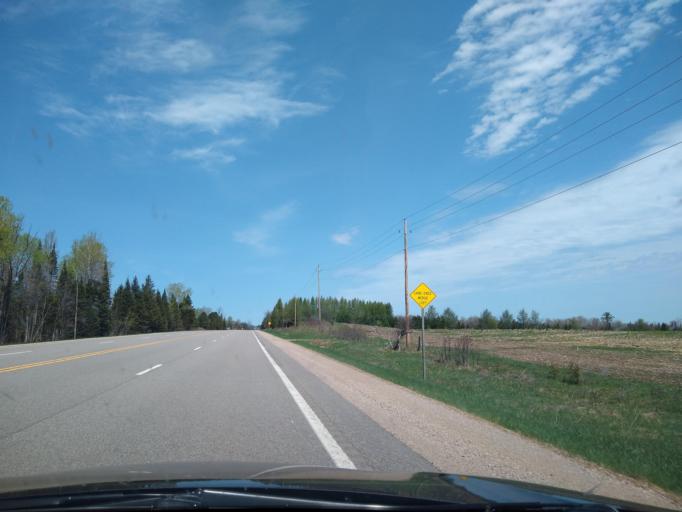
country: US
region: Michigan
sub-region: Delta County
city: Gladstone
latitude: 46.0917
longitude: -86.9807
